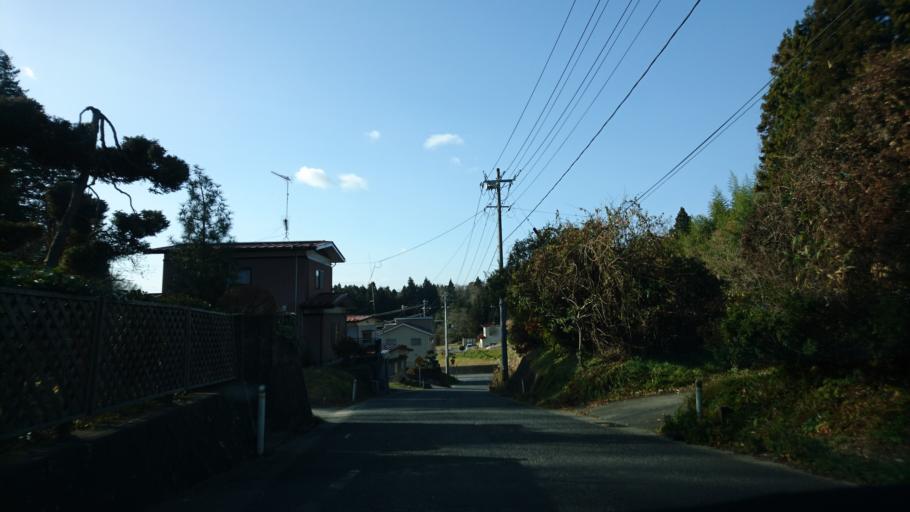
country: JP
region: Iwate
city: Ichinoseki
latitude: 38.9123
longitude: 141.3386
